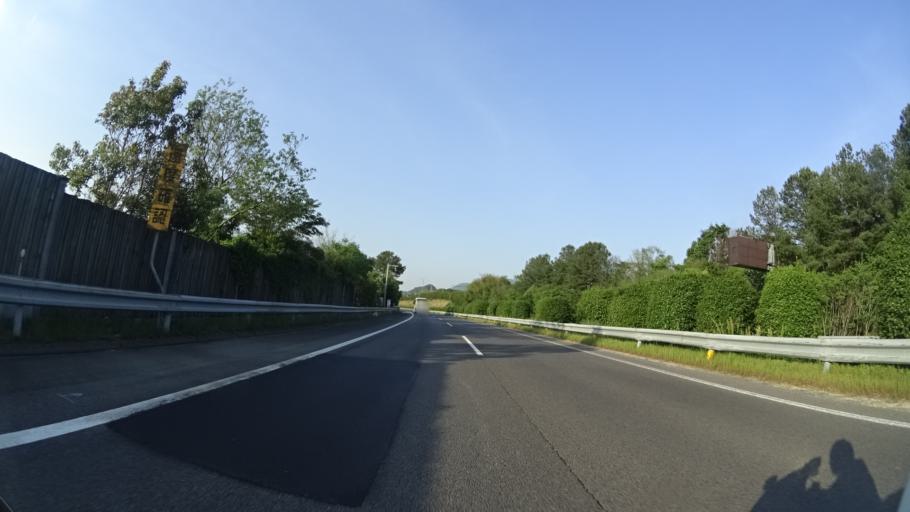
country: JP
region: Kagawa
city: Kan'onjicho
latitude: 34.1594
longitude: 133.7269
